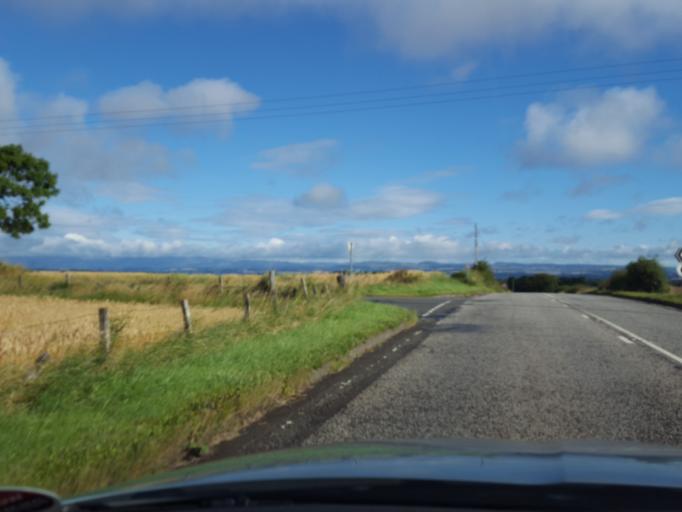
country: GB
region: Scotland
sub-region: West Lothian
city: Broxburn
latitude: 55.9537
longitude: -3.5096
